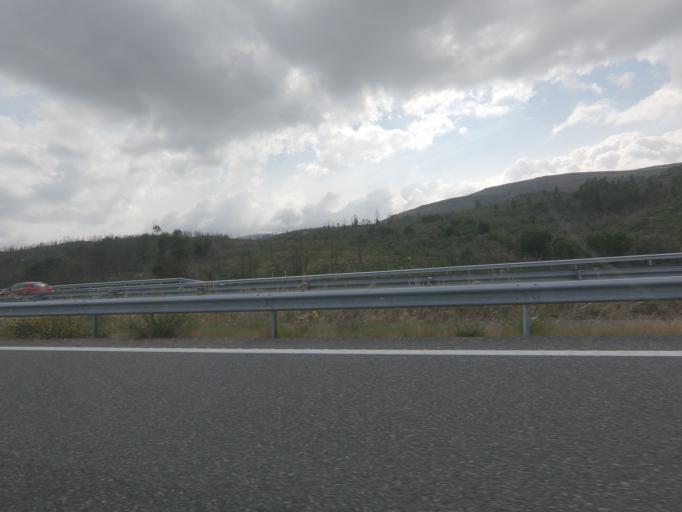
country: ES
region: Galicia
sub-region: Provincia de Ourense
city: Melon
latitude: 42.2758
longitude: -8.2031
